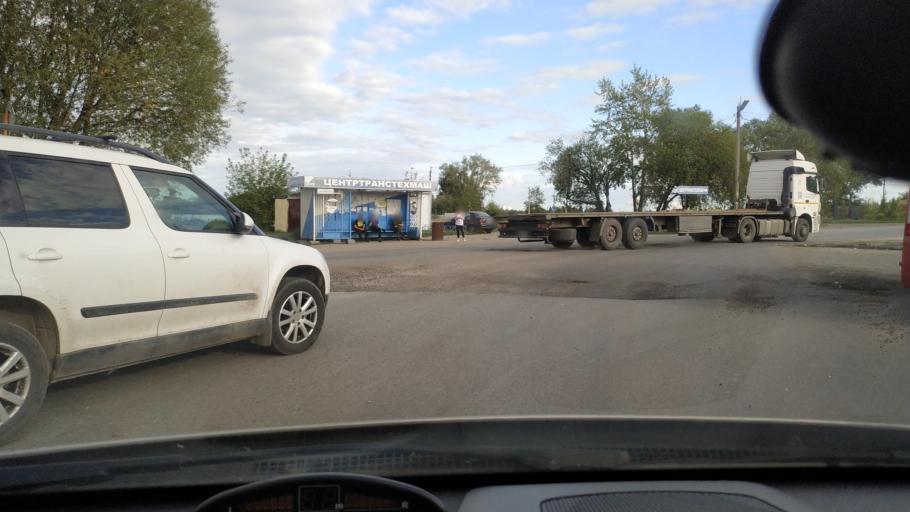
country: RU
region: Rjazan
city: Polyany
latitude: 54.5837
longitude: 39.8392
